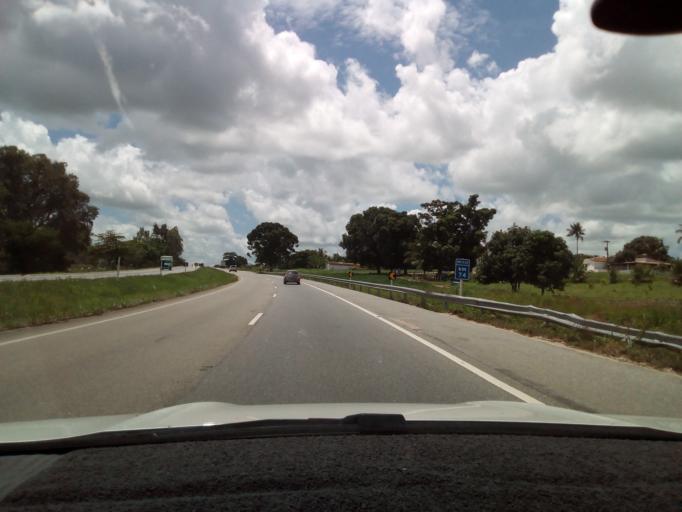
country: BR
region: Paraiba
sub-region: Pilar
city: Pilar
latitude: -7.1910
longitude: -35.2691
